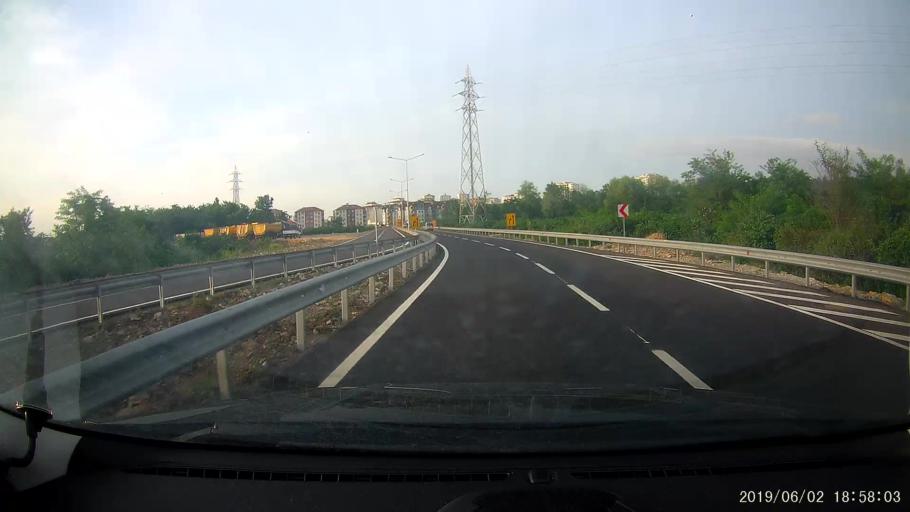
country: TR
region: Ordu
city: Ordu
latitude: 40.9569
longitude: 37.9037
